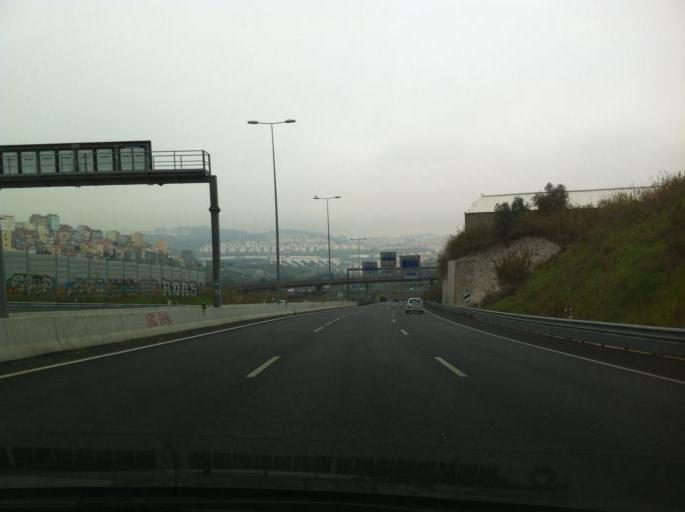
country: PT
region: Lisbon
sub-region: Odivelas
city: Pontinha
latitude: 38.7658
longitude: -9.2050
